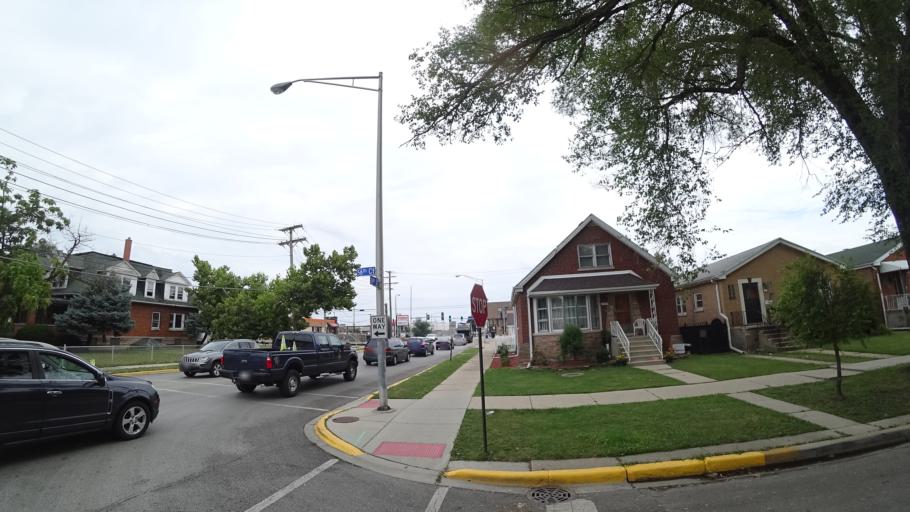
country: US
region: Illinois
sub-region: Cook County
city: Cicero
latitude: 41.8581
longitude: -87.7654
